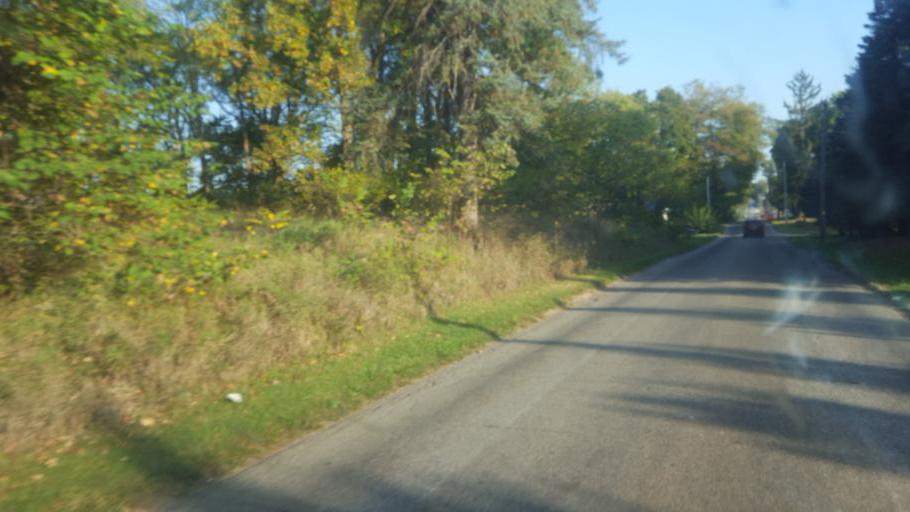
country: US
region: Indiana
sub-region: LaGrange County
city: Lagrange
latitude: 41.6373
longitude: -85.4248
